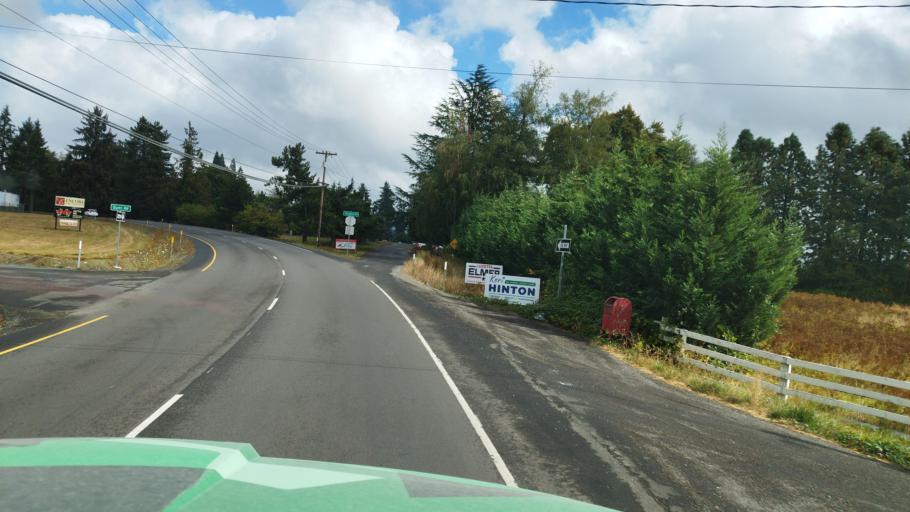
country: US
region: Oregon
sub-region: Yamhill County
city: Lafayette
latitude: 45.2341
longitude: -123.1526
